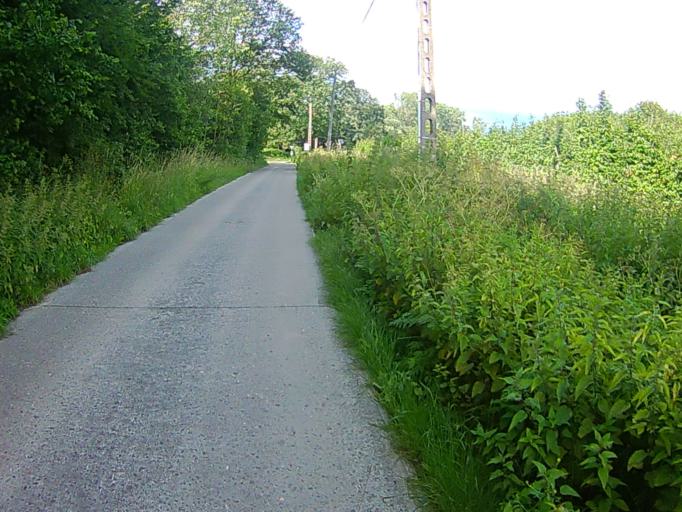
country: BE
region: Flanders
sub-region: Provincie Antwerpen
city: Berlaar
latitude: 51.1199
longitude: 4.6919
